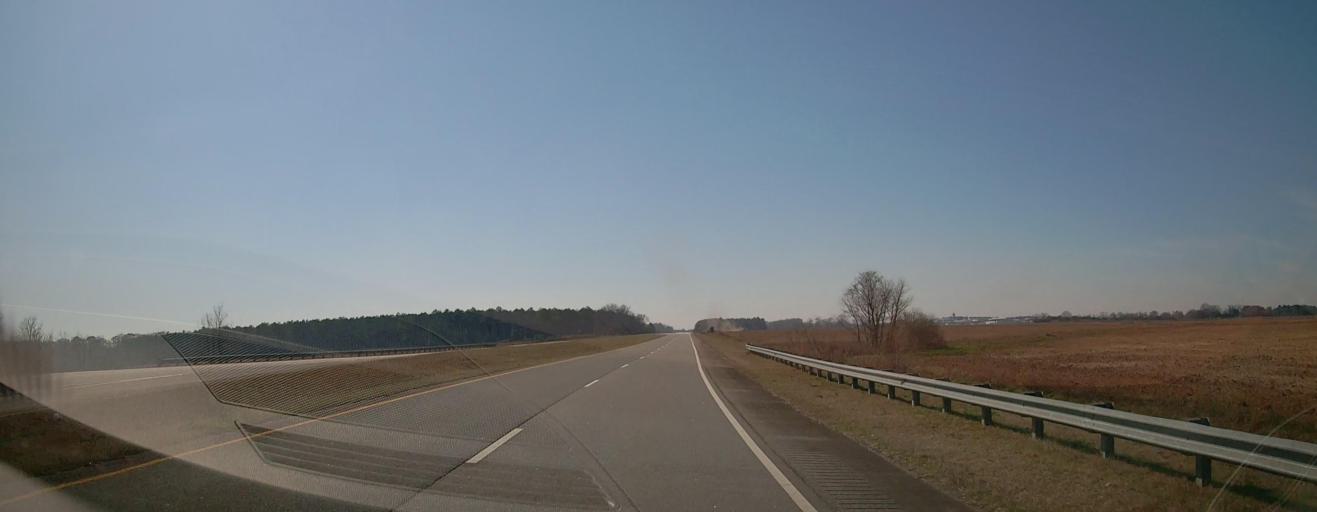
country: US
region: Georgia
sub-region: Houston County
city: Perry
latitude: 32.4303
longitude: -83.7258
